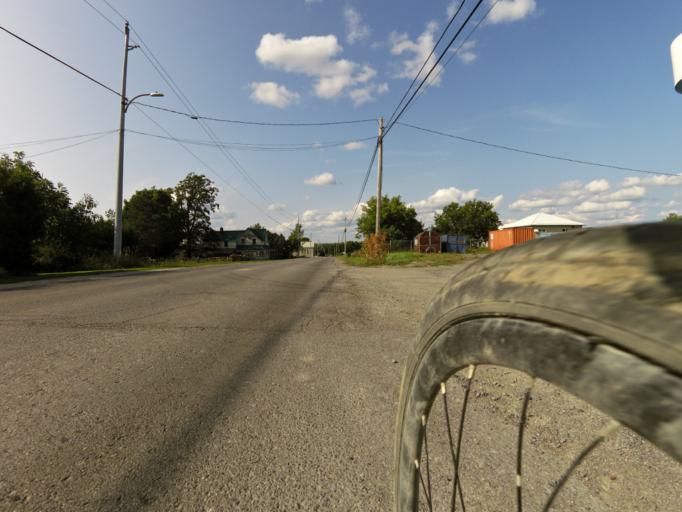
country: CA
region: Ontario
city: Kingston
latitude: 44.4030
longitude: -76.5963
